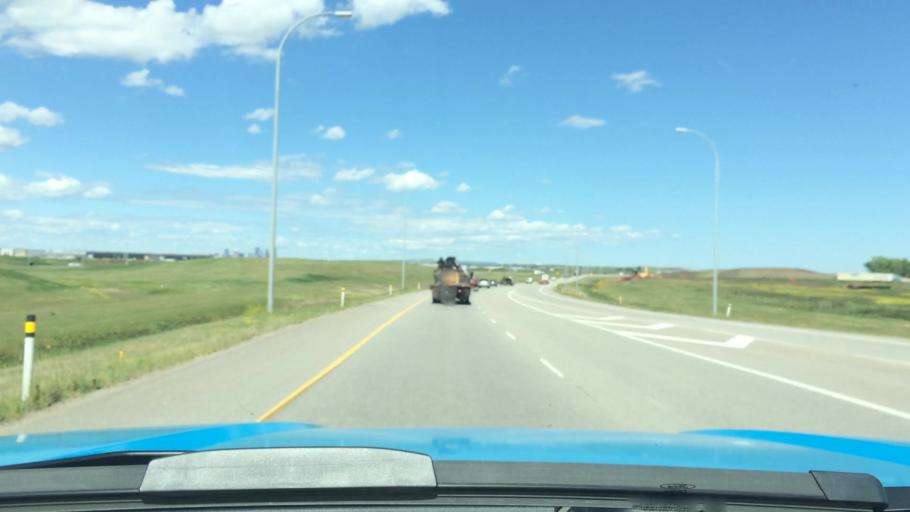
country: CA
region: Alberta
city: Chestermere
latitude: 50.9811
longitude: -113.9157
